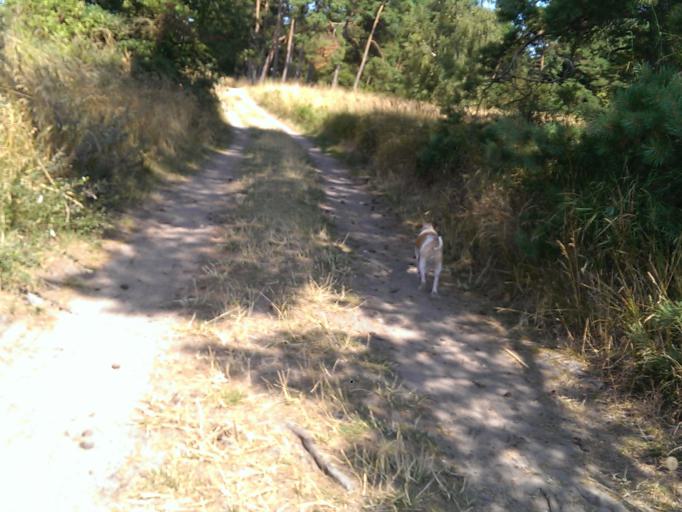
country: SE
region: Skane
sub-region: Simrishamns Kommun
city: Simrishamn
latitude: 55.4274
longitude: 14.2217
